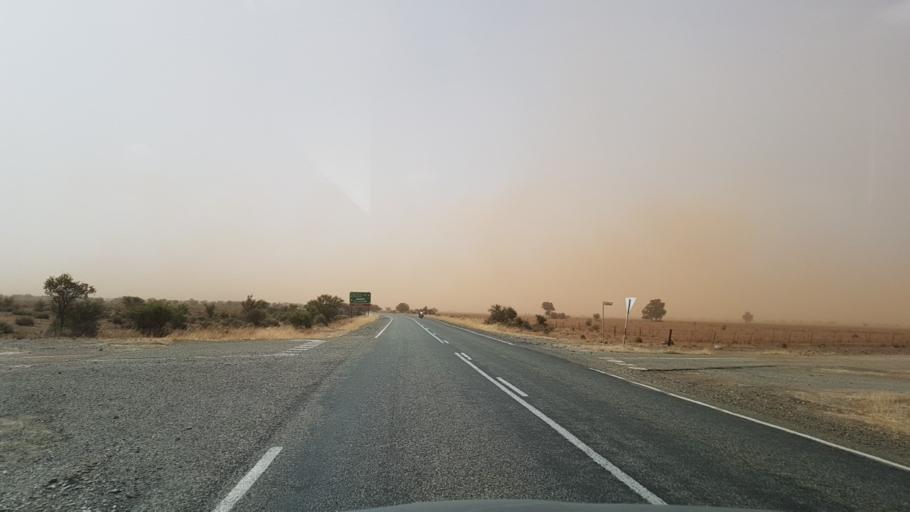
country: AU
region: South Australia
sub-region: Peterborough
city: Peterborough
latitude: -33.1389
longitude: 138.9323
